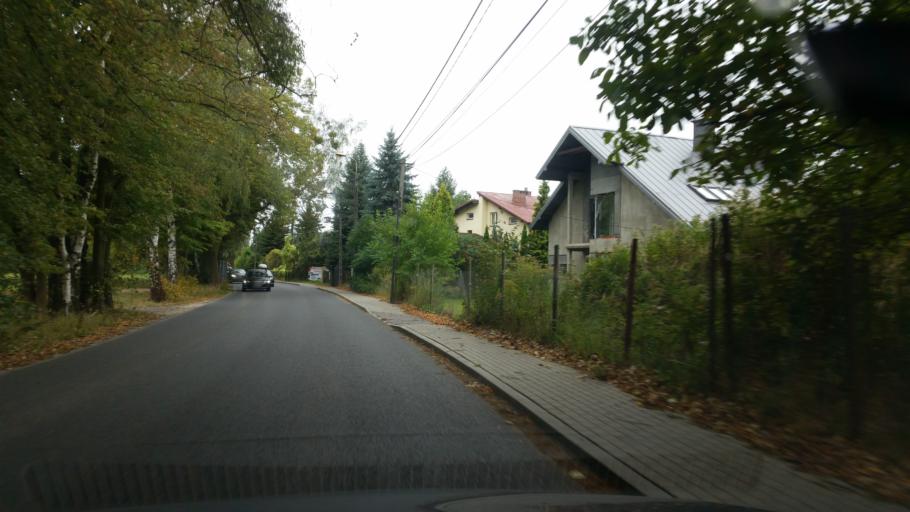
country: PL
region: Masovian Voivodeship
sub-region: Warszawa
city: Kabaty
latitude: 52.1033
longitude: 21.0873
